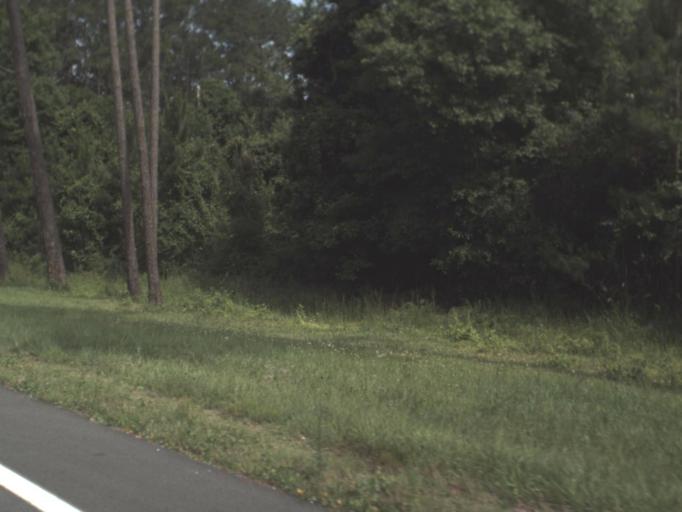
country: US
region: Florida
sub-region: Bradford County
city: Starke
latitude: 29.9386
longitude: -82.0735
